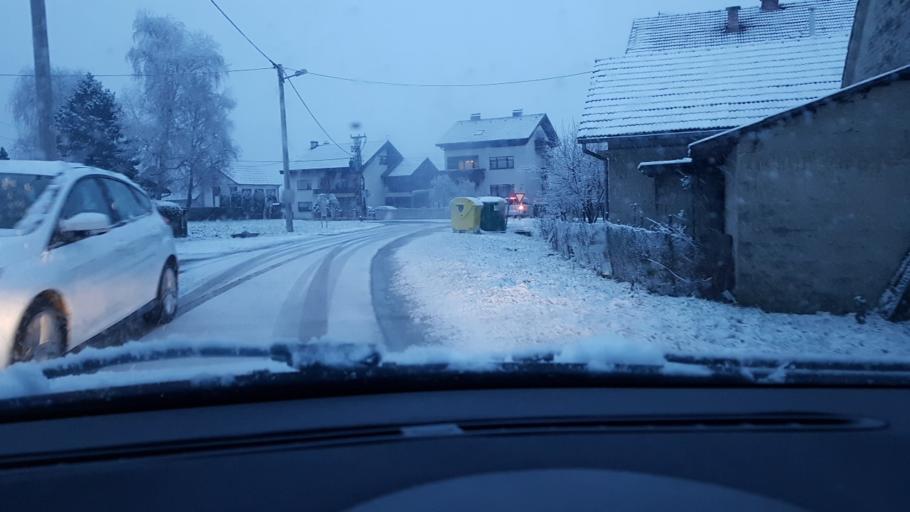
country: HR
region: Krapinsko-Zagorska
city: Zabok
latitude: 46.0170
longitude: 15.8789
